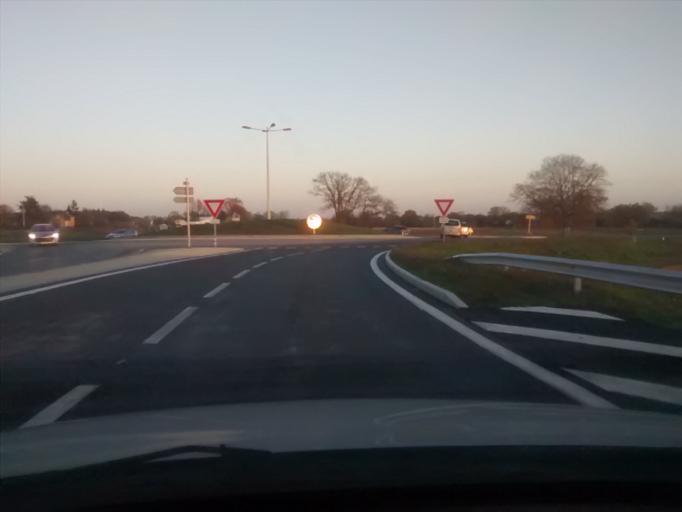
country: FR
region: Pays de la Loire
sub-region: Departement de la Mayenne
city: Loiron
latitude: 48.0716
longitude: -0.8948
